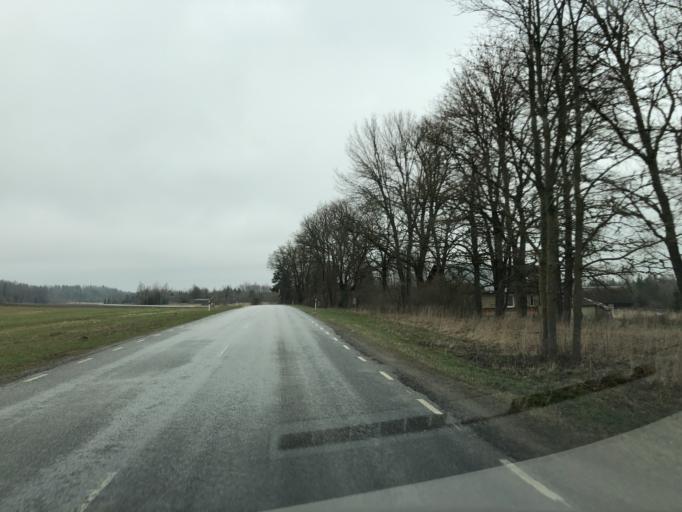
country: EE
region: Laeaene-Virumaa
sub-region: Rakke vald
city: Rakke
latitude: 58.9660
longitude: 26.2777
